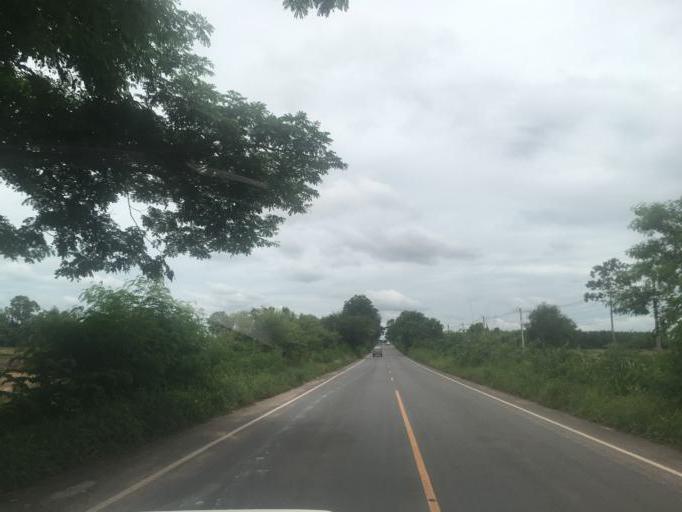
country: TH
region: Changwat Udon Thani
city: Udon Thani
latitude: 17.3121
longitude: 102.7104
